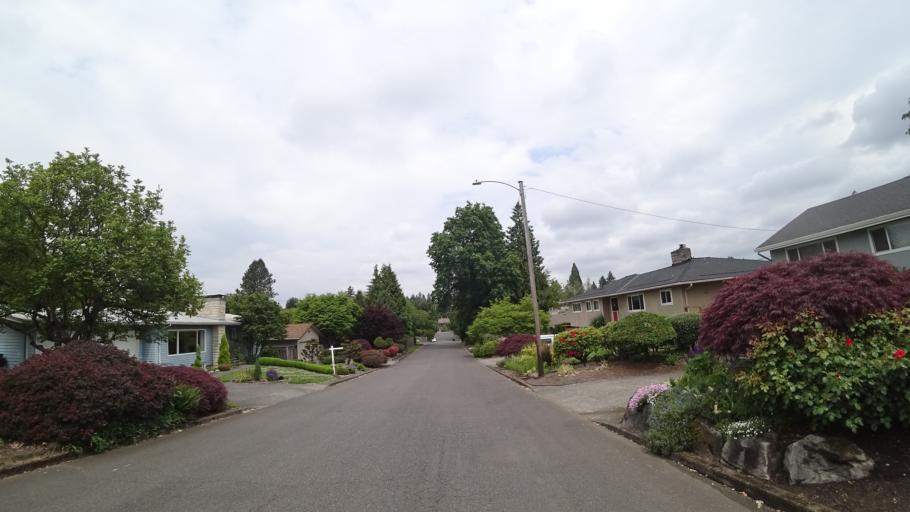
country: US
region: Oregon
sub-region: Clackamas County
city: Milwaukie
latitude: 45.4854
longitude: -122.6299
